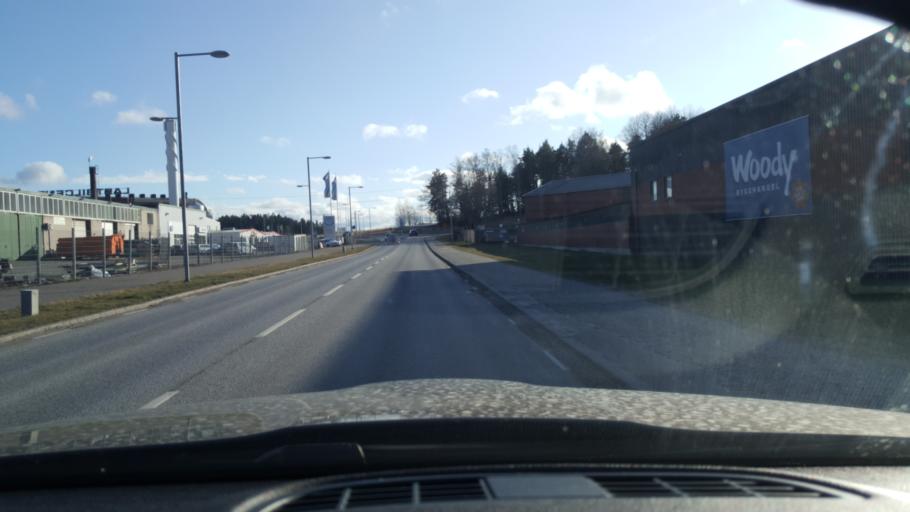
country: SE
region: Stockholm
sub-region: Osterakers Kommun
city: Akersberga
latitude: 59.4928
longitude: 18.2766
